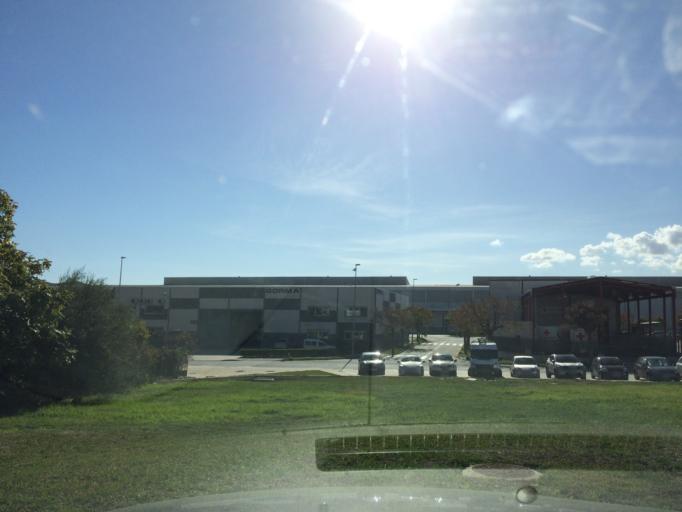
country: ES
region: Andalusia
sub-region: Provincia de Malaga
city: Estacion de Cartama
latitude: 36.7342
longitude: -4.5451
